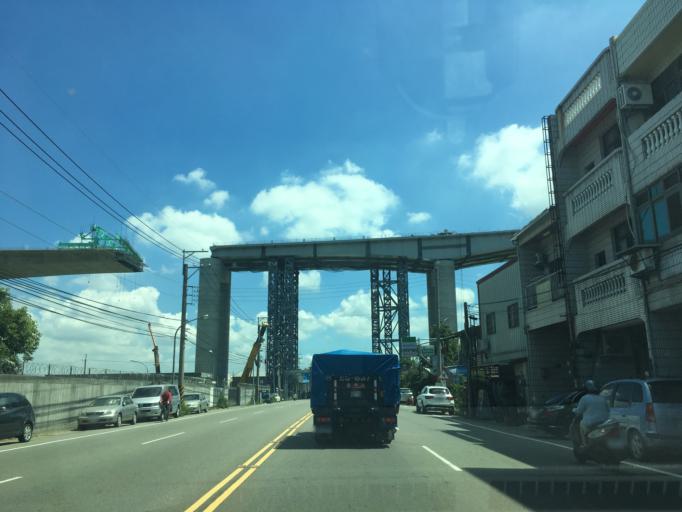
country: TW
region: Taiwan
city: Fengyuan
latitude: 24.2193
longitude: 120.7238
